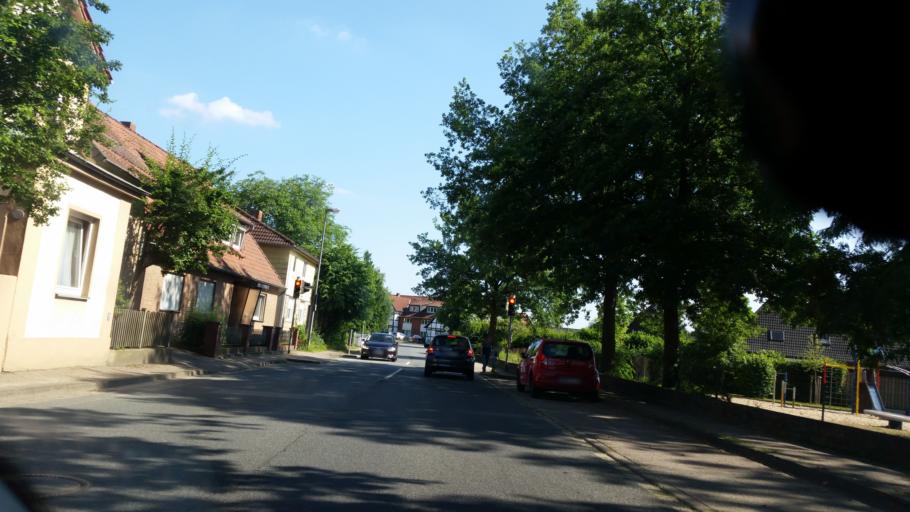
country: DE
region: Lower Saxony
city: Wolfsburg
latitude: 52.3491
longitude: 10.7787
